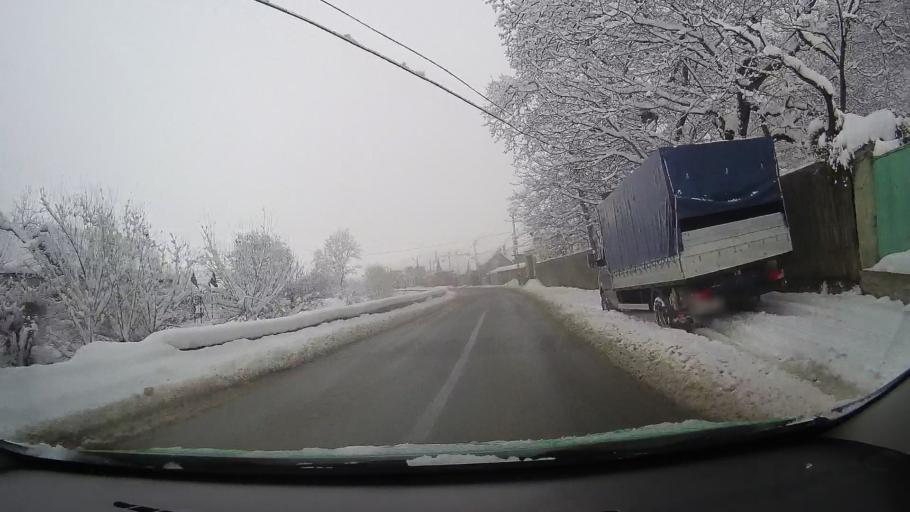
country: RO
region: Sibiu
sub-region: Oras Saliste
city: Saliste
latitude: 45.7945
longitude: 23.8747
